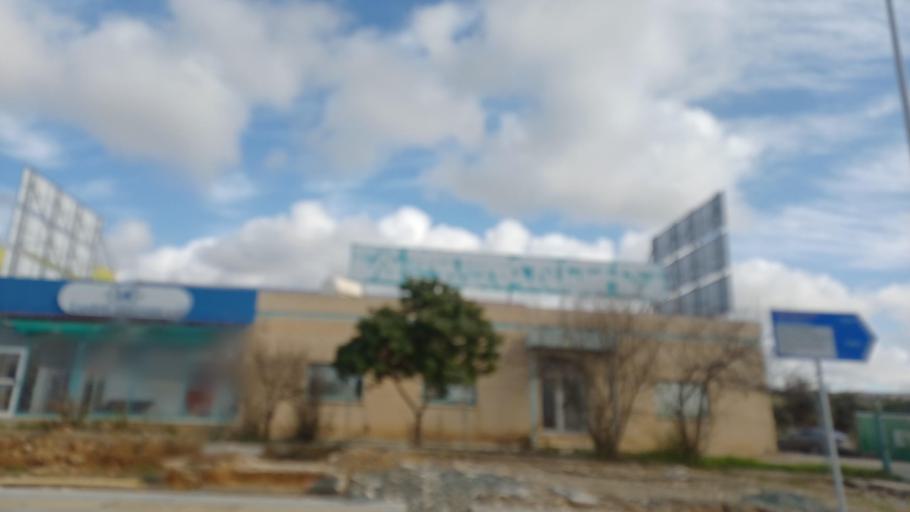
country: CY
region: Pafos
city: Paphos
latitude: 34.7748
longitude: 32.4473
